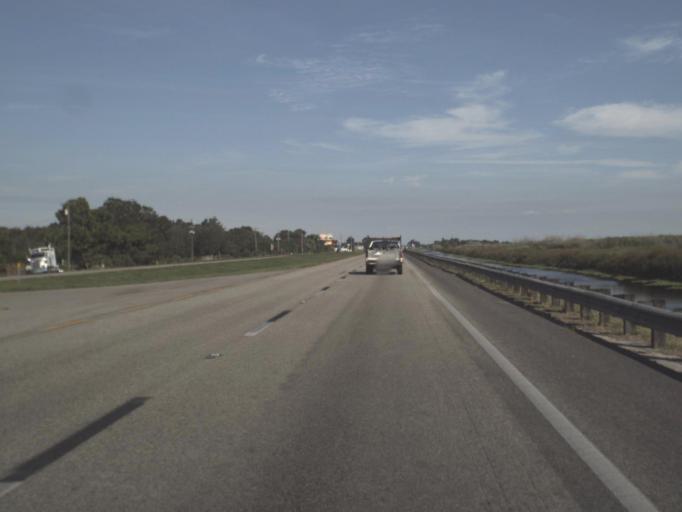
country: US
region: Florida
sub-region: Hendry County
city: Harlem
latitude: 26.7541
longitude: -80.9865
